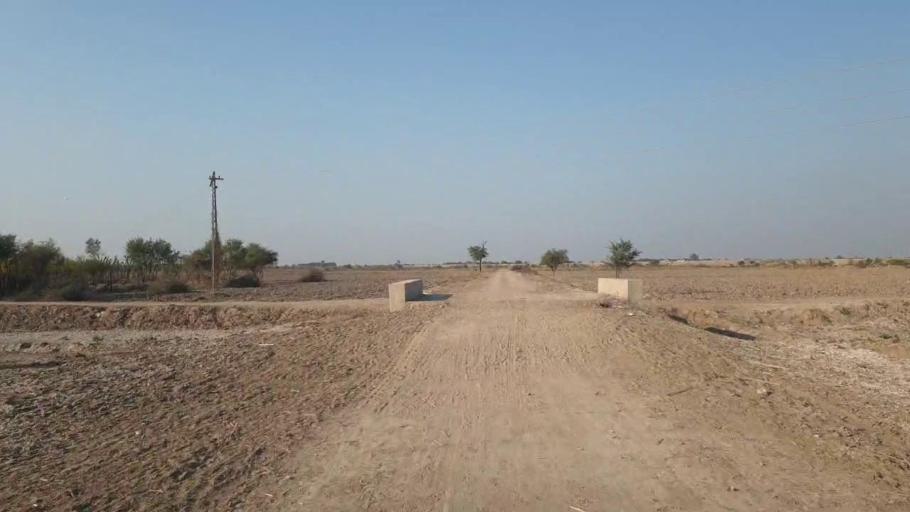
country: PK
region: Sindh
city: Mirpur Khas
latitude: 25.4531
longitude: 68.9333
